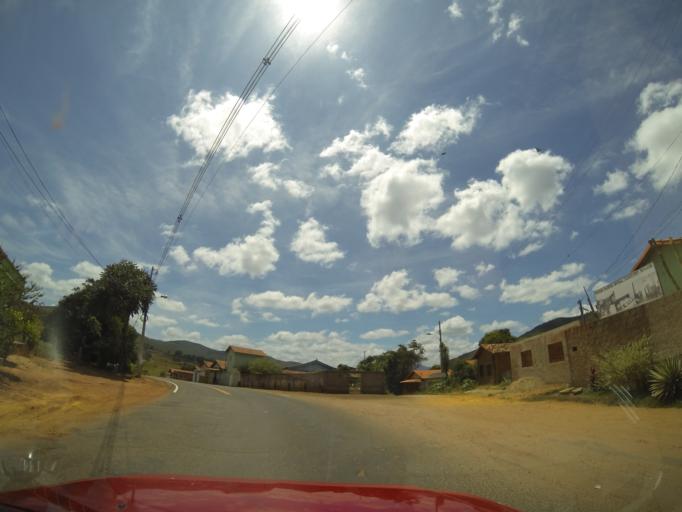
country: BR
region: Minas Gerais
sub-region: Diamantina
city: Diamantina
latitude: -18.0752
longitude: -43.4693
